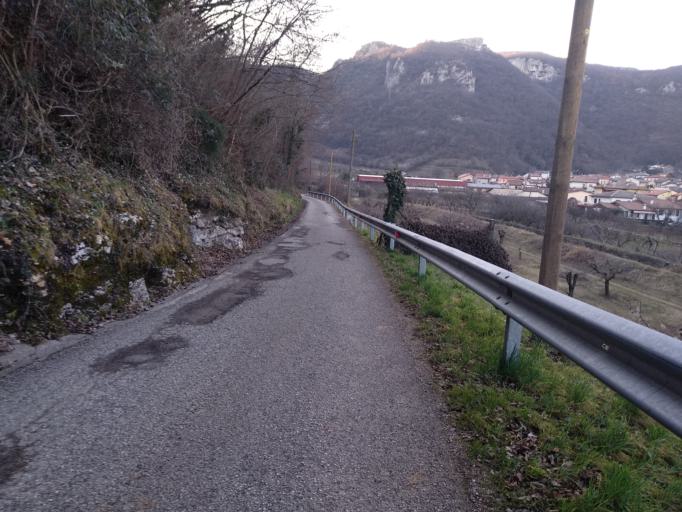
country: IT
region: Veneto
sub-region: Provincia di Vicenza
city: Lumignano
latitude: 45.4571
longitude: 11.5847
